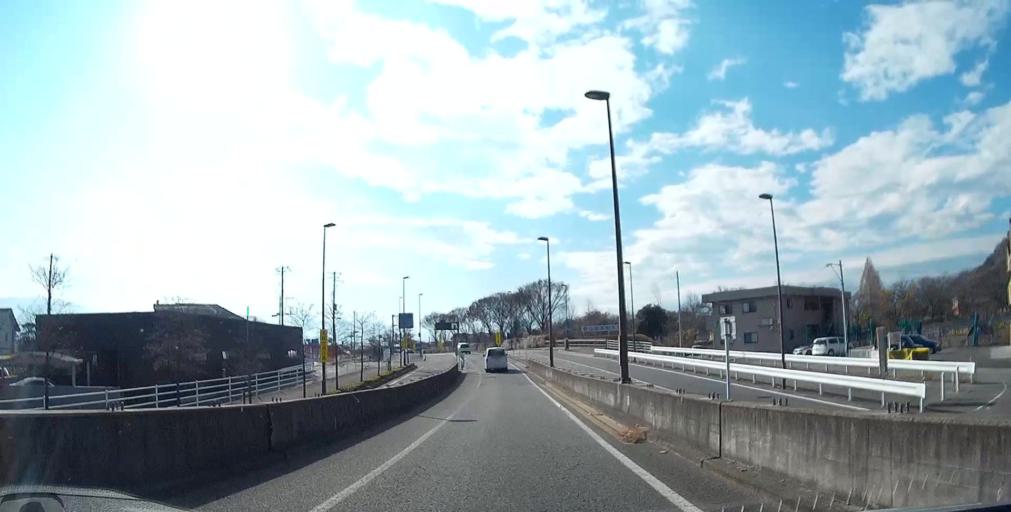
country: JP
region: Yamanashi
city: Isawa
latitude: 35.6610
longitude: 138.6163
